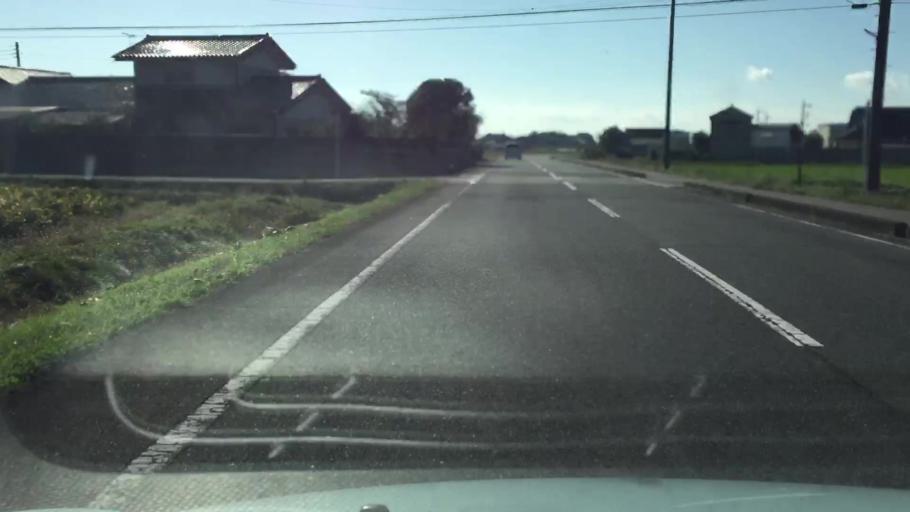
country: JP
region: Tochigi
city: Ujiie
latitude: 36.6713
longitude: 140.0166
